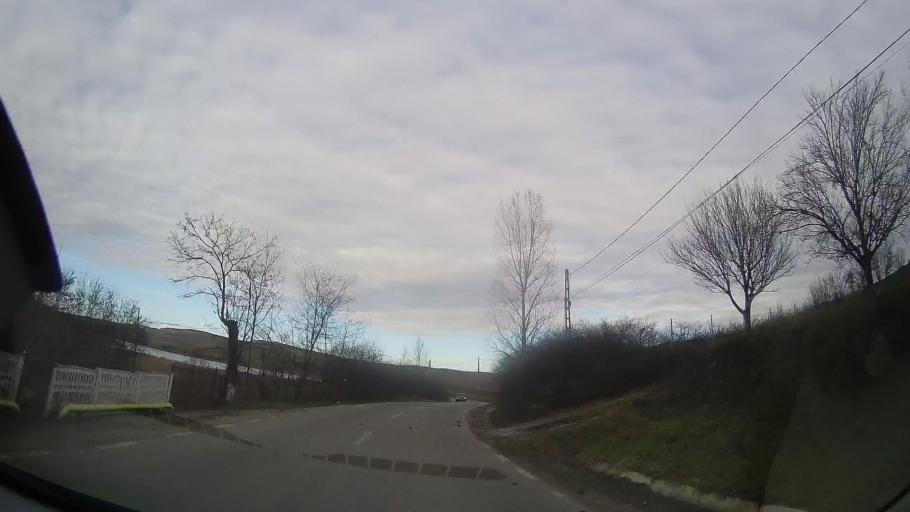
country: RO
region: Cluj
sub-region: Comuna Geaca
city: Geaca
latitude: 46.8347
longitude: 24.1340
